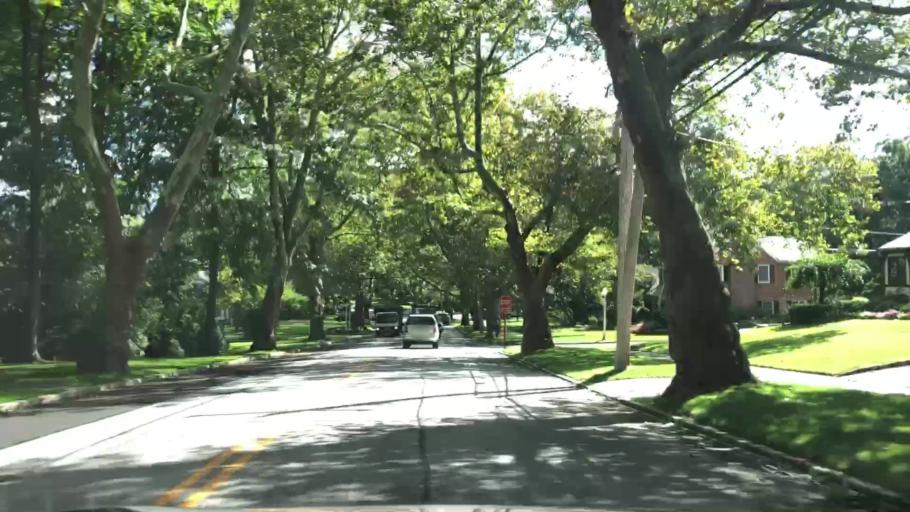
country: US
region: New York
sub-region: Nassau County
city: Munsey Park
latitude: 40.8003
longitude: -73.6834
